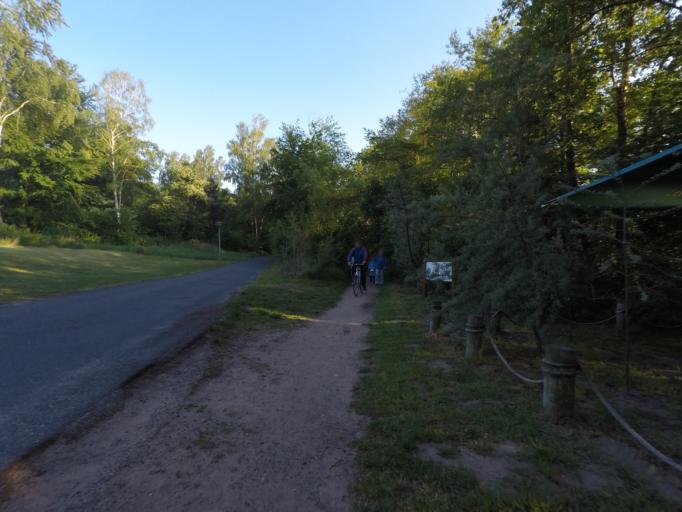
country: DE
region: Brandenburg
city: Joachimsthal
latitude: 52.9208
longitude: 13.7244
